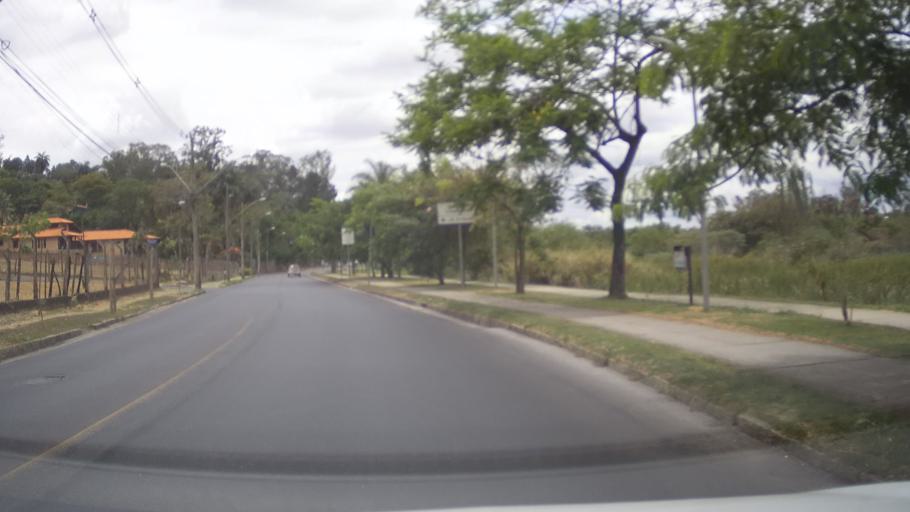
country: BR
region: Minas Gerais
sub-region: Contagem
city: Contagem
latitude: -19.8509
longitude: -44.0040
